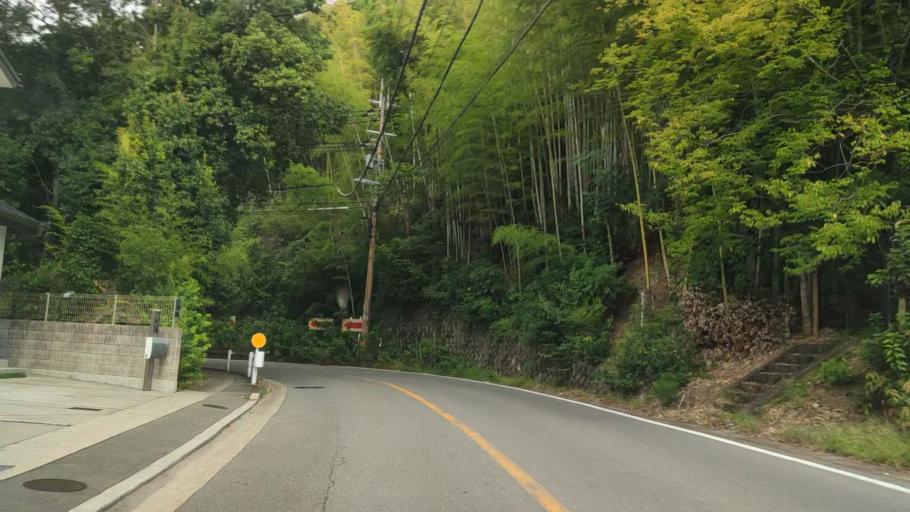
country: JP
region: Kyoto
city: Kyoto
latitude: 35.0239
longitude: 135.6984
